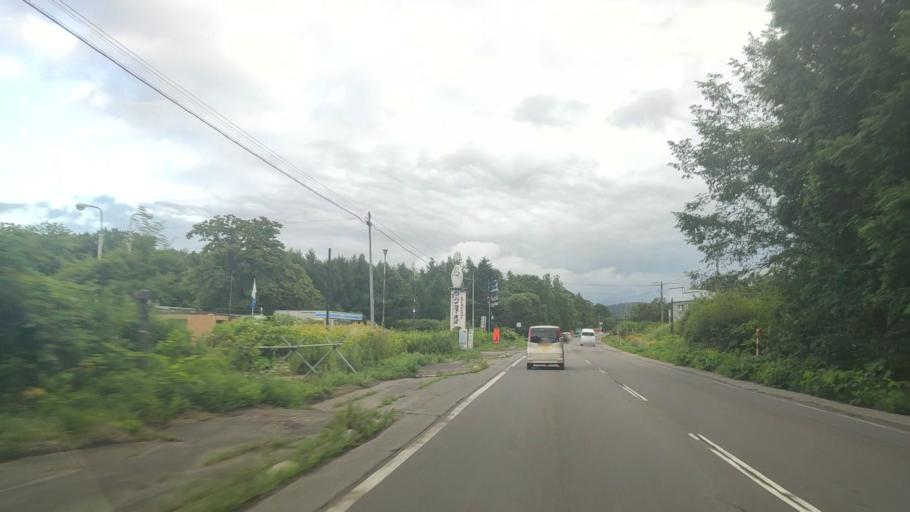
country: JP
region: Hokkaido
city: Nanae
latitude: 41.9991
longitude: 140.6353
